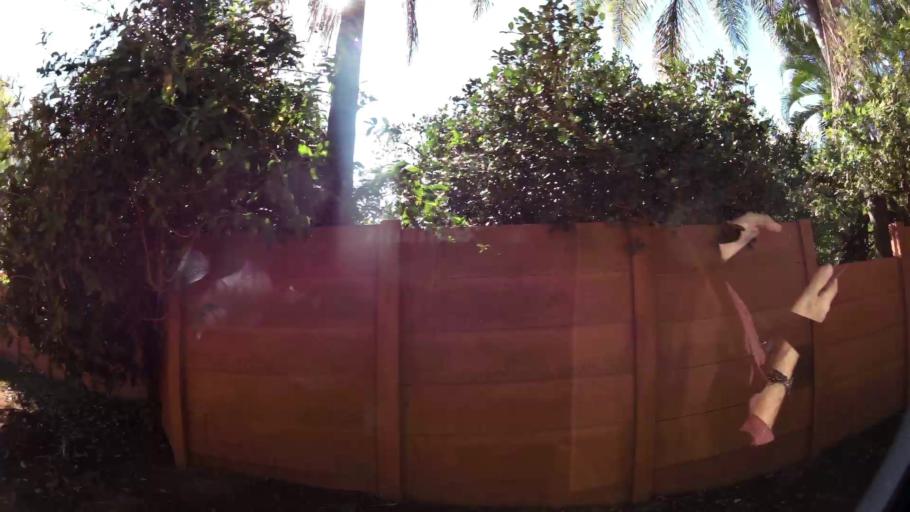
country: ZA
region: Limpopo
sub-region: Mopani District Municipality
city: Tzaneen
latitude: -23.8198
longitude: 30.1564
